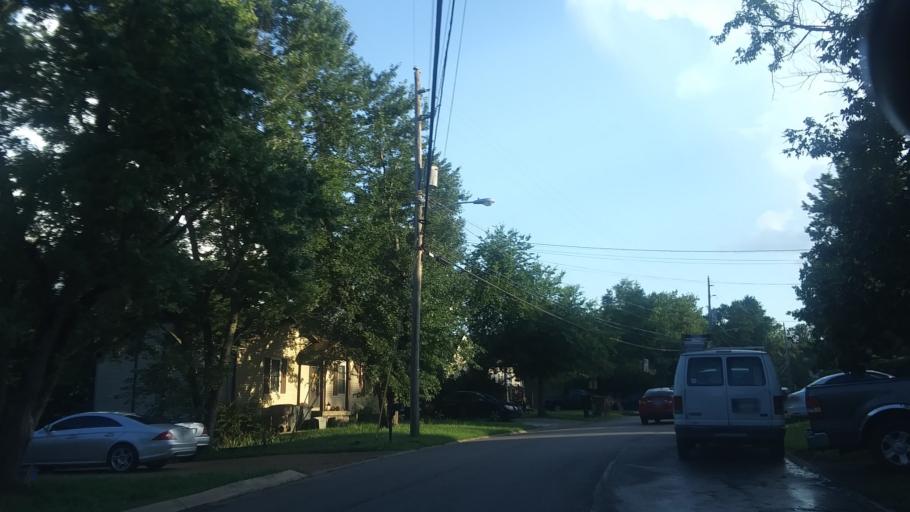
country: US
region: Tennessee
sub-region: Rutherford County
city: La Vergne
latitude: 36.0737
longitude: -86.6691
